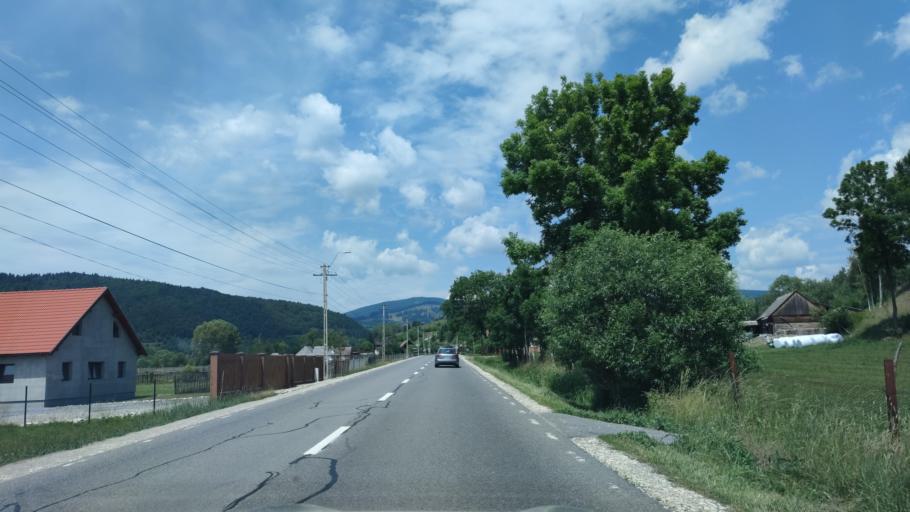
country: RO
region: Harghita
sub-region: Comuna Sandominic
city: Sandominic
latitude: 46.6051
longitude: 25.7527
